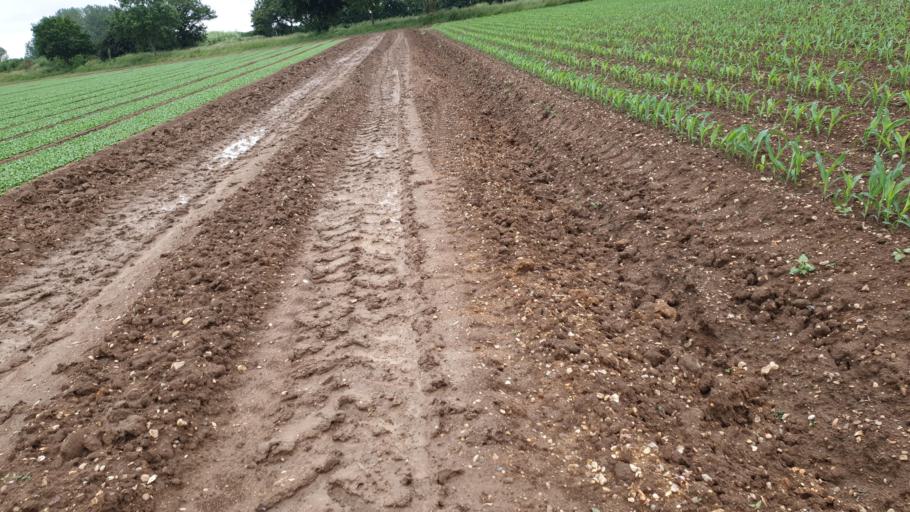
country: GB
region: England
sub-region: Essex
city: Great Bentley
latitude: 51.8608
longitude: 1.0412
